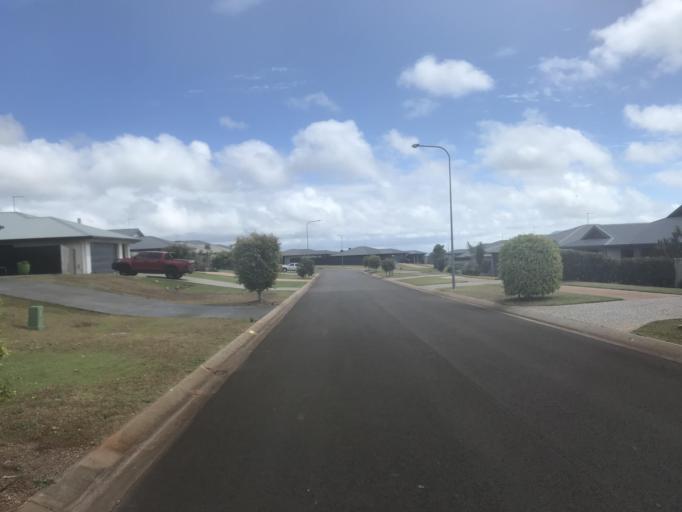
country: AU
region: Queensland
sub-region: Tablelands
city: Tolga
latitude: -17.2205
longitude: 145.4750
